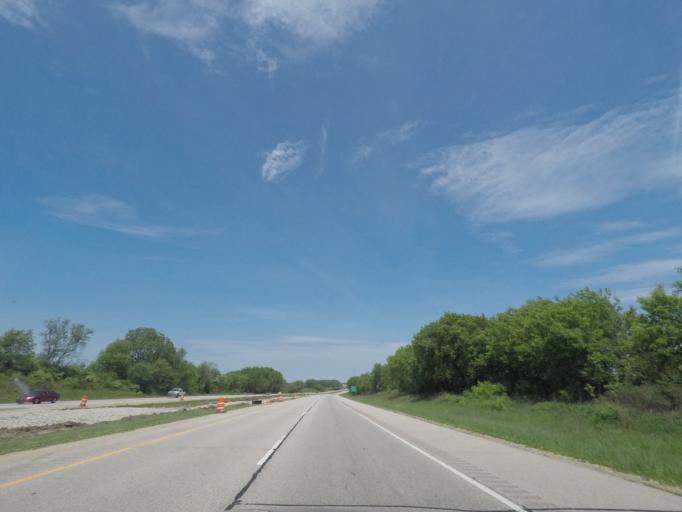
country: US
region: Wisconsin
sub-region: Dane County
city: Oregon
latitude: 42.9924
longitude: -89.3860
